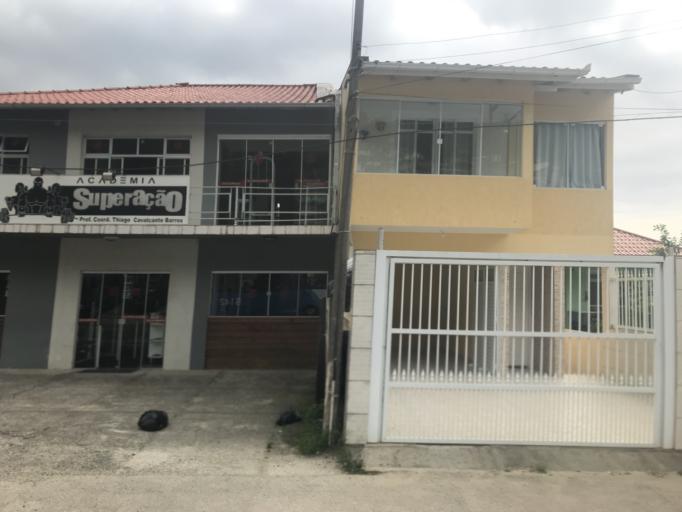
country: BR
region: Santa Catarina
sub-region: Florianopolis
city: Costeira do Pirajubae
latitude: -27.6373
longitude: -48.5223
